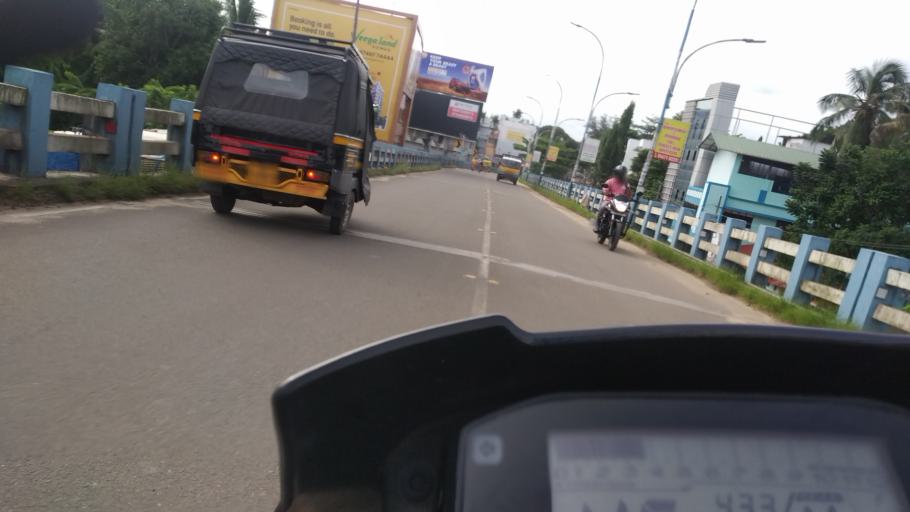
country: IN
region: Kerala
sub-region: Ernakulam
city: Cochin
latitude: 9.9768
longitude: 76.3146
